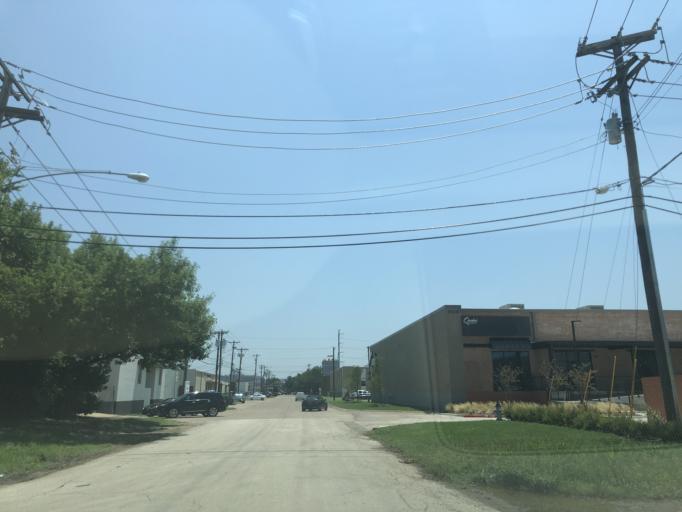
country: US
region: Texas
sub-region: Dallas County
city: Dallas
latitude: 32.8014
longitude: -96.8470
